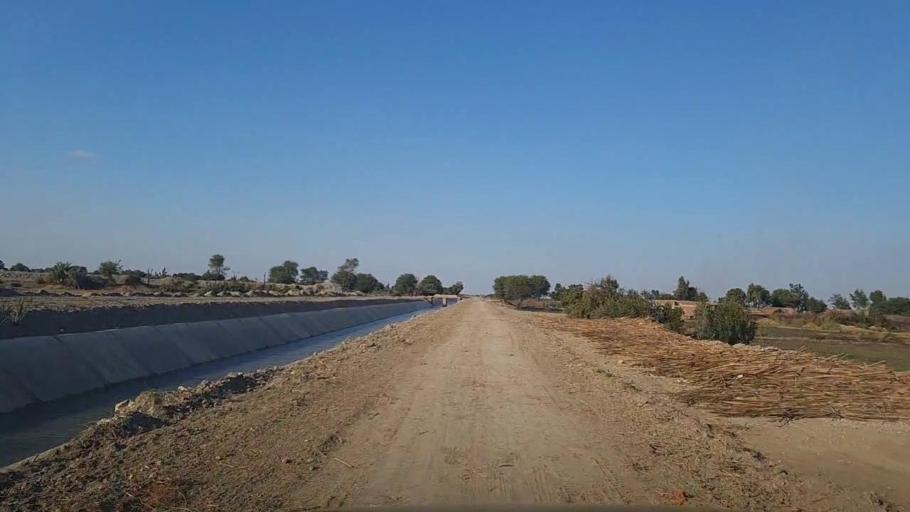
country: PK
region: Sindh
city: Jhol
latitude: 25.9100
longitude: 69.0401
